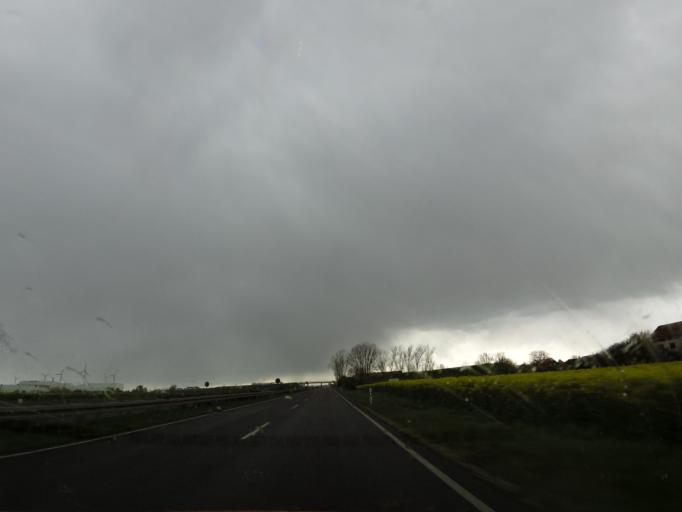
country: DE
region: Saxony-Anhalt
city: Hohendodeleben
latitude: 52.0335
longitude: 11.5181
